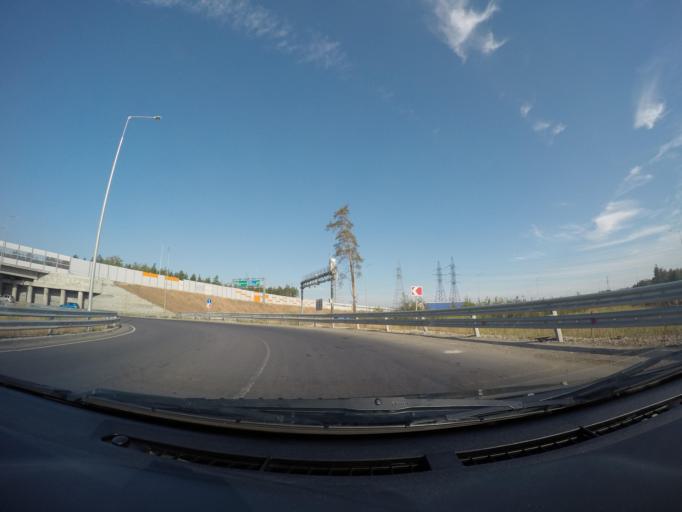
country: RU
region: Moskovskaya
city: Gzhel'
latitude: 55.6338
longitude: 38.3630
